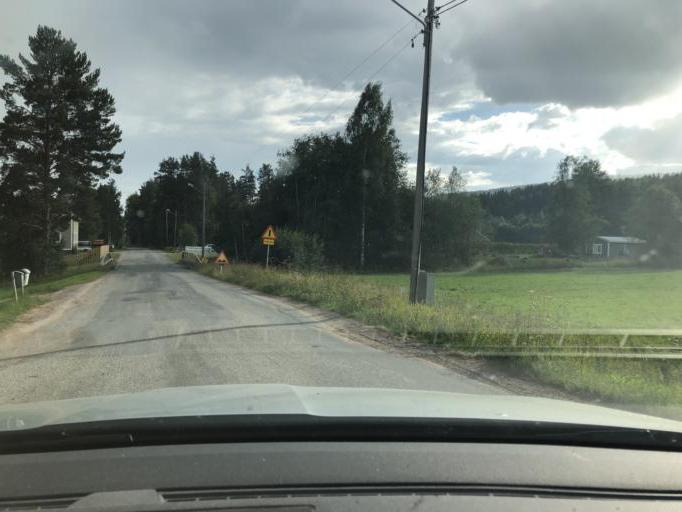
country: SE
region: Vaesternorrland
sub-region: Solleftea Kommun
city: Solleftea
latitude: 63.2461
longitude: 17.1900
